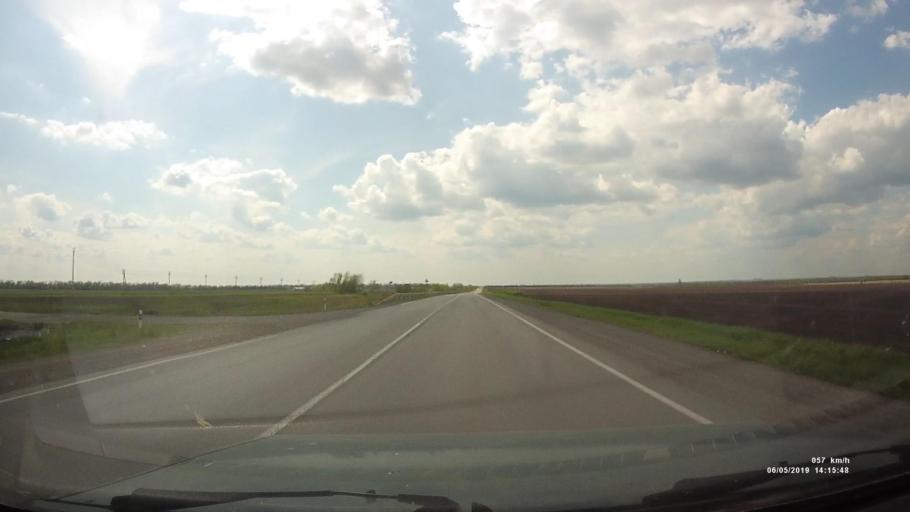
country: RU
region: Rostov
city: Kamenolomni
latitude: 47.6353
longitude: 40.2995
